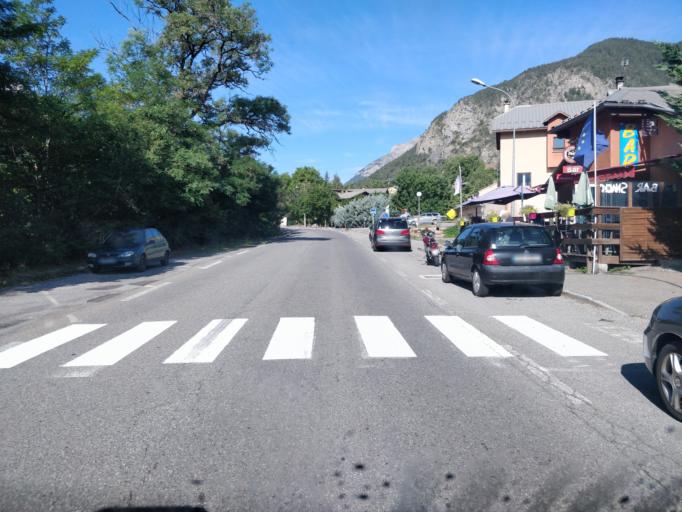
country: FR
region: Provence-Alpes-Cote d'Azur
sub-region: Departement des Alpes-de-Haute-Provence
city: Barcelonnette
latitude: 44.3934
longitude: 6.5732
